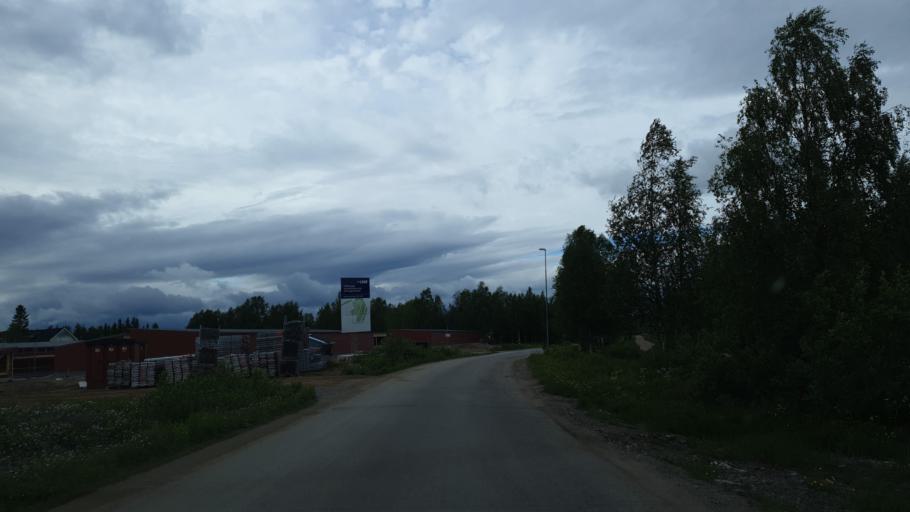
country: SE
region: Norrbotten
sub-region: Gallivare Kommun
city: Gaellivare
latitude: 67.1282
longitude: 20.6508
